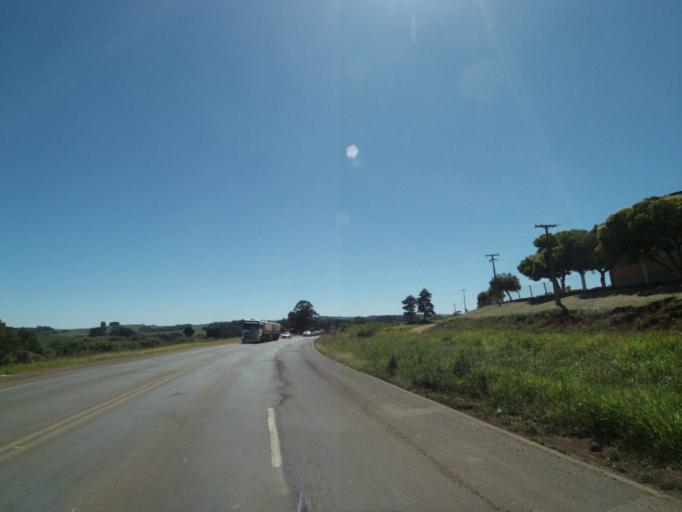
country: BR
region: Parana
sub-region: Pato Branco
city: Pato Branco
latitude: -26.2564
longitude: -52.7848
